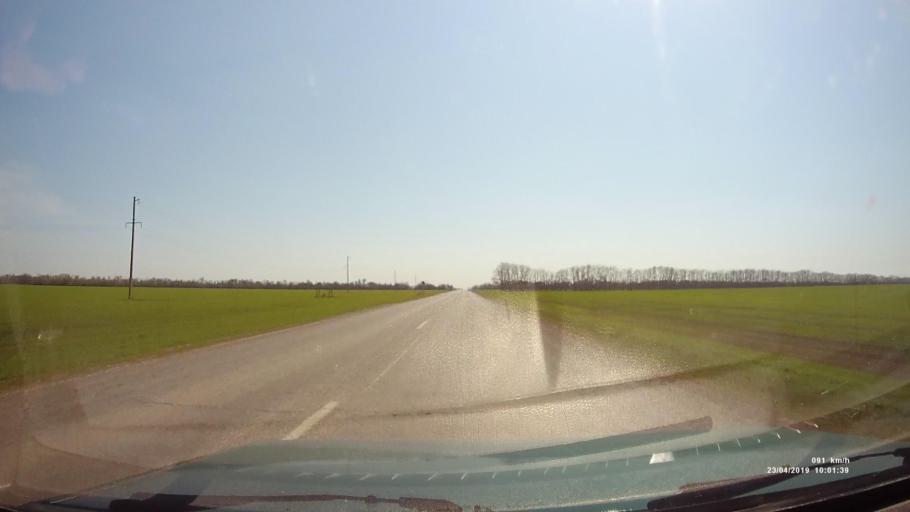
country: RU
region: Rostov
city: Sovetskoye
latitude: 46.7646
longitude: 42.1540
